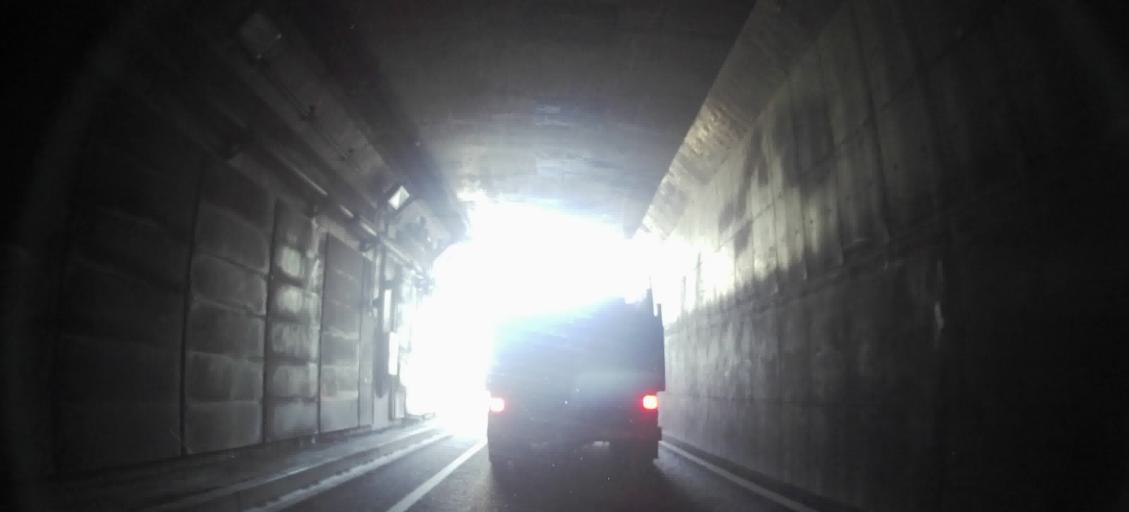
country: JP
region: Saitama
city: Wako
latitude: 35.7338
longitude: 139.6146
